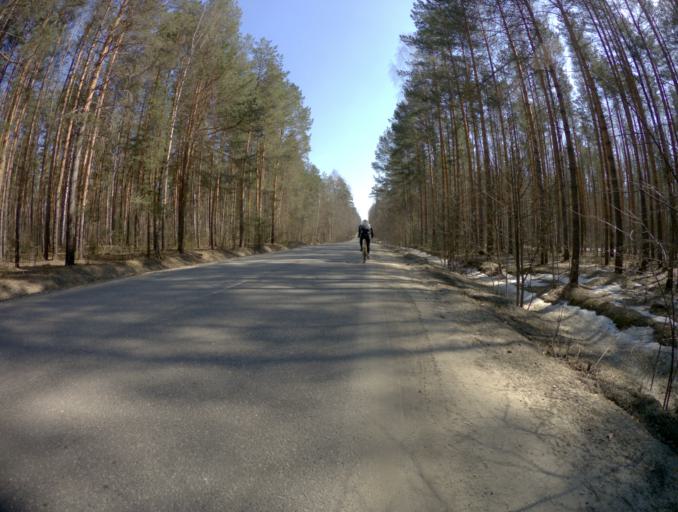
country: RU
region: Vladimir
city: Bogolyubovo
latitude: 56.1549
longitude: 40.5451
